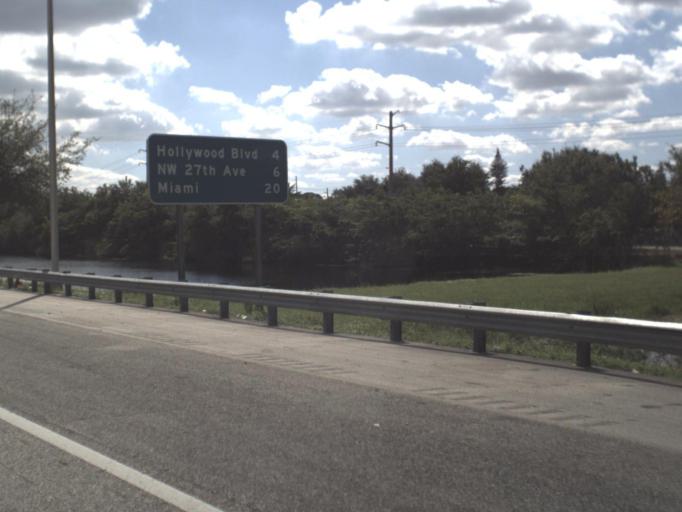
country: US
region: Florida
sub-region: Broward County
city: Davie
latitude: 26.0511
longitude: -80.2150
